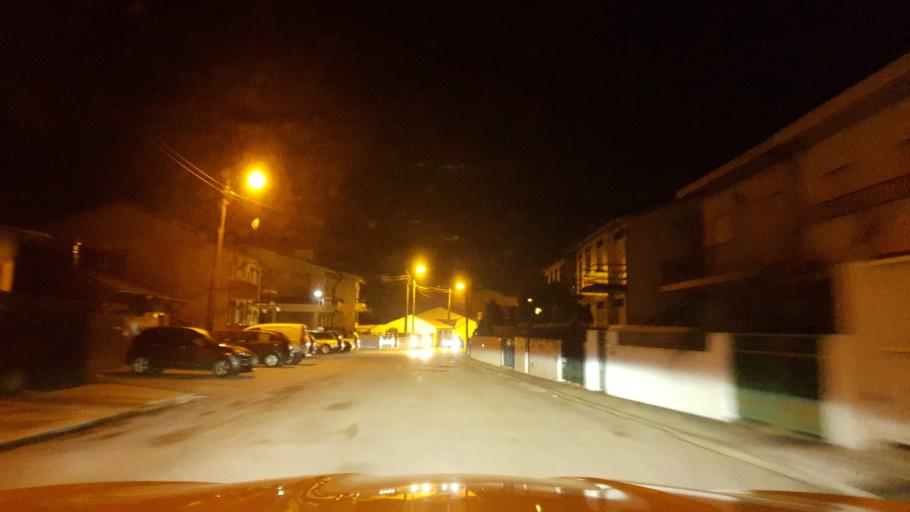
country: PT
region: Porto
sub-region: Maia
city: Leca do Bailio
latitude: 41.2100
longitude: -8.6367
